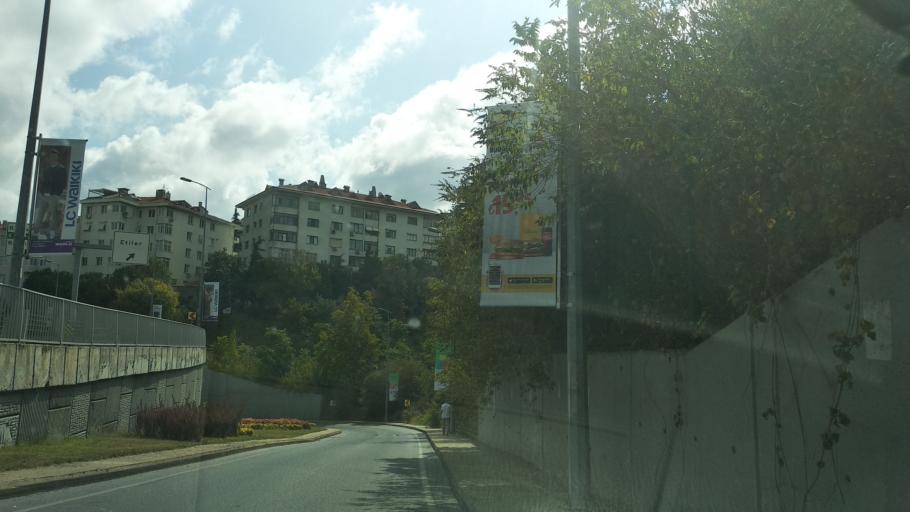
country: TR
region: Istanbul
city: Sisli
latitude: 41.0894
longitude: 29.0392
